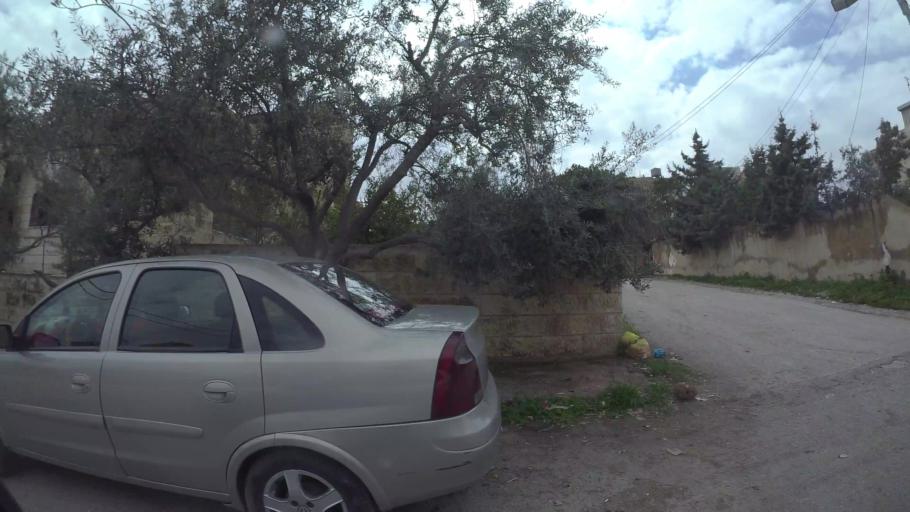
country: JO
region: Amman
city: Al Jubayhah
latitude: 32.0554
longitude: 35.8314
